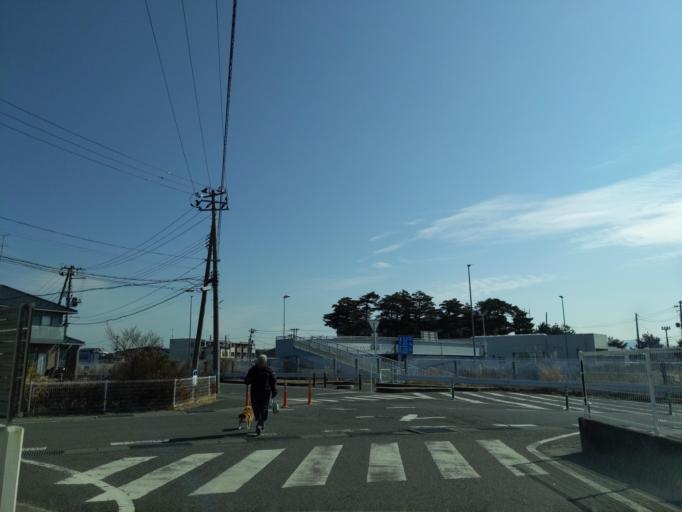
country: JP
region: Fukushima
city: Koriyama
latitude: 37.4237
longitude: 140.3568
